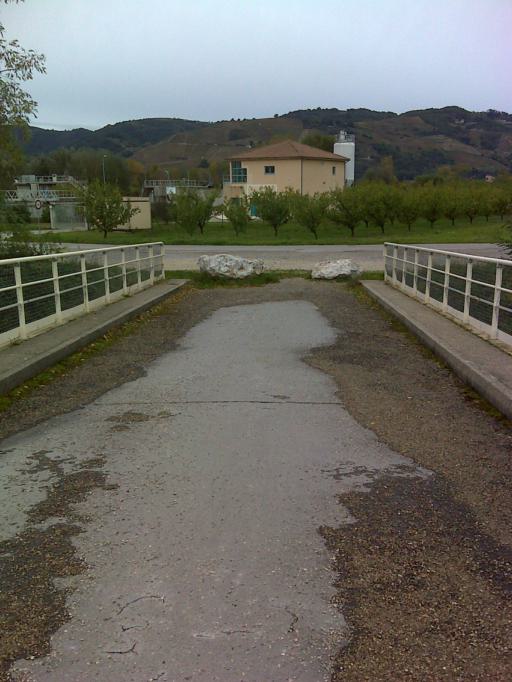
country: FR
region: Rhone-Alpes
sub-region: Departement de l'Ardeche
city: Mauves
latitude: 45.0429
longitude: 4.8440
